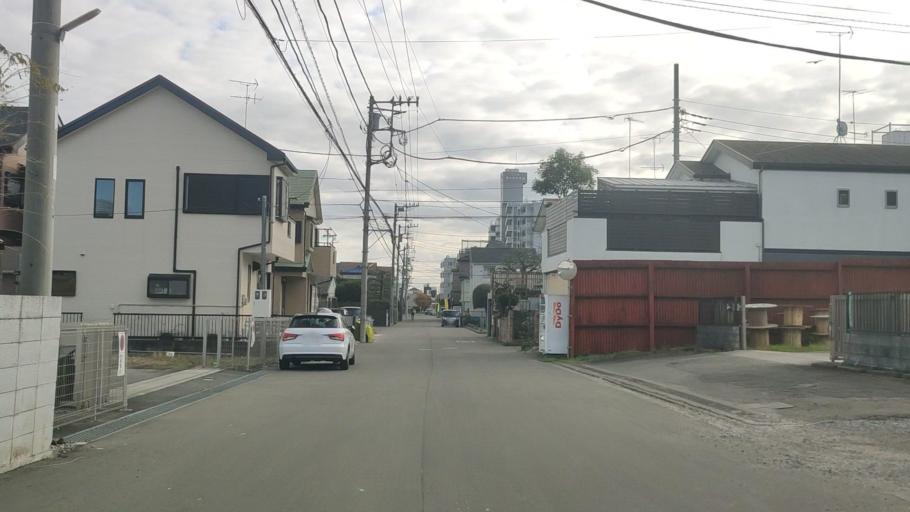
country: JP
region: Kanagawa
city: Minami-rinkan
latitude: 35.4963
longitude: 139.4328
